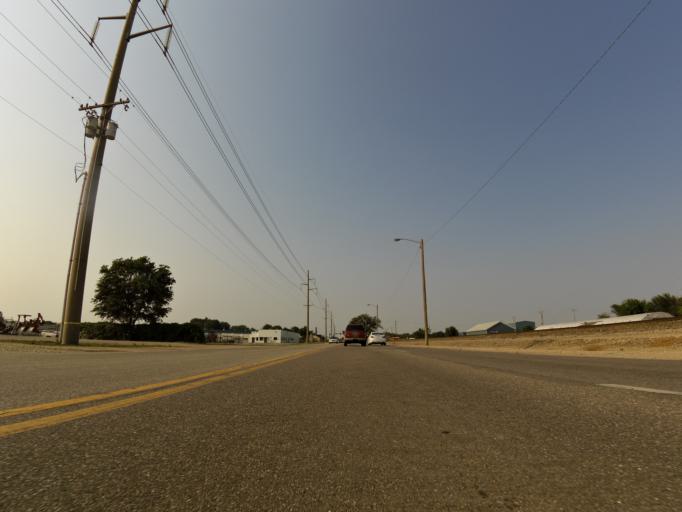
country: US
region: Kansas
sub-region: Sedgwick County
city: Park City
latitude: 37.7498
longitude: -97.3360
